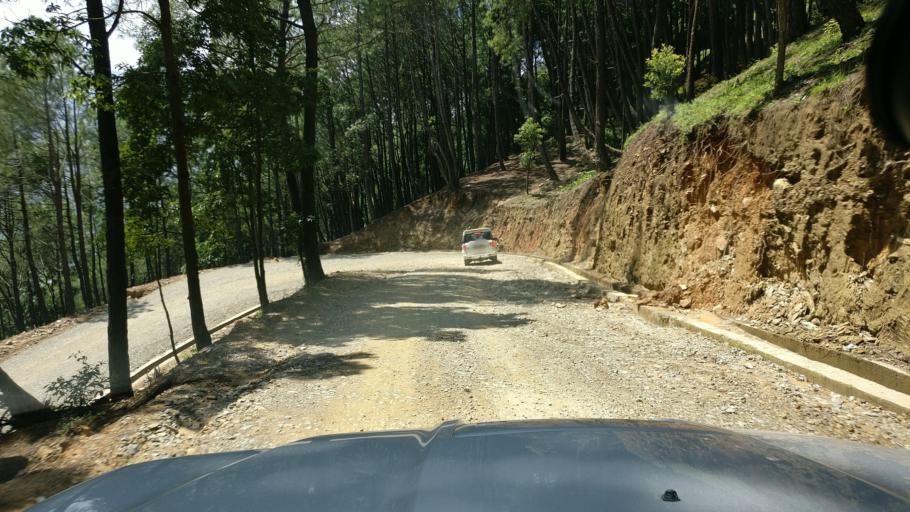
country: NP
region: Central Region
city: Kirtipur
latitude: 27.7056
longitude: 85.2486
